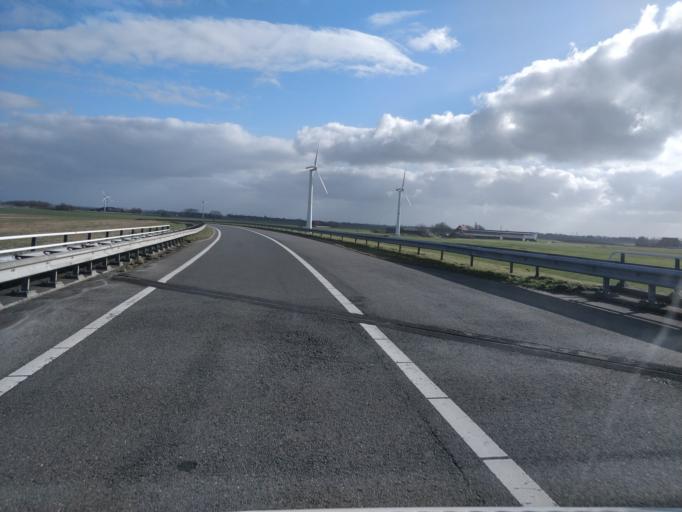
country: NL
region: Friesland
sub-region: Sudwest Fryslan
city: Makkum
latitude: 53.0969
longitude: 5.3926
